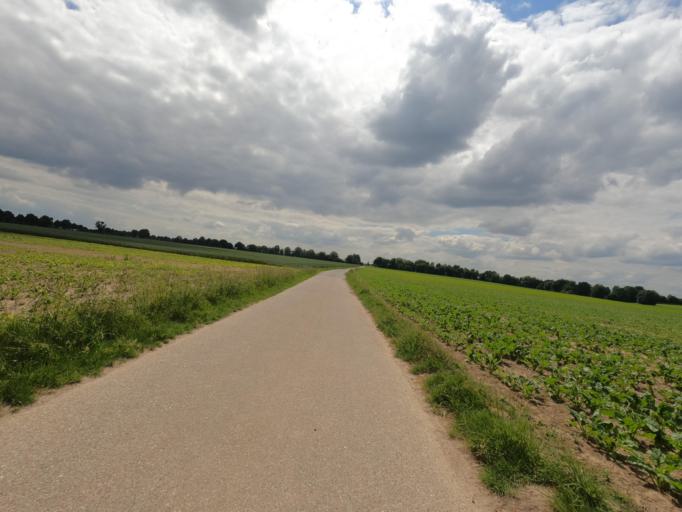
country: DE
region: North Rhine-Westphalia
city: Geilenkirchen
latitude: 50.9581
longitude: 6.0887
